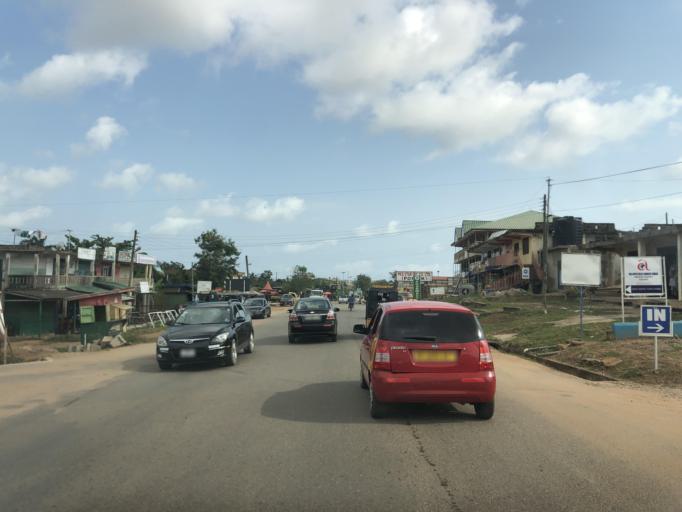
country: GH
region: Central
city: Cape Coast
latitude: 5.1417
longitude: -1.2831
